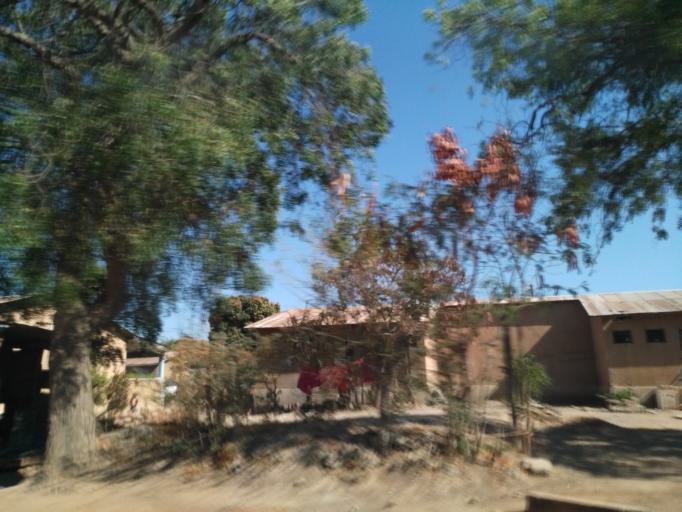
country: TZ
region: Dodoma
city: Dodoma
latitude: -6.1603
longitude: 35.7513
